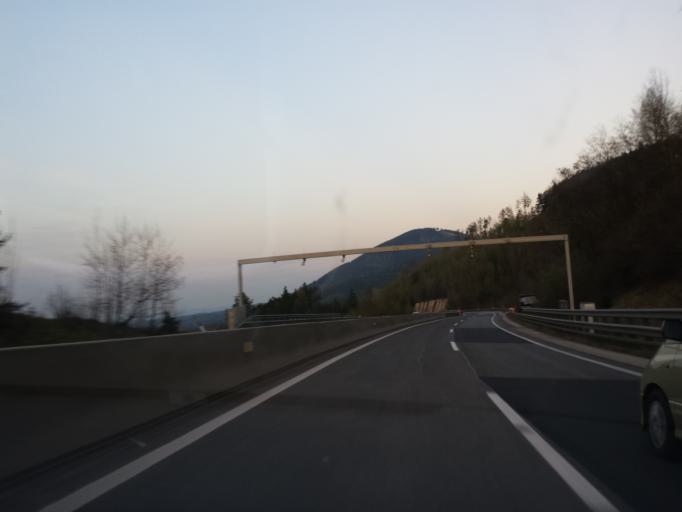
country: AT
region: Lower Austria
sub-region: Politischer Bezirk Neunkirchen
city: Schottwien
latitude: 47.6555
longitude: 15.8998
